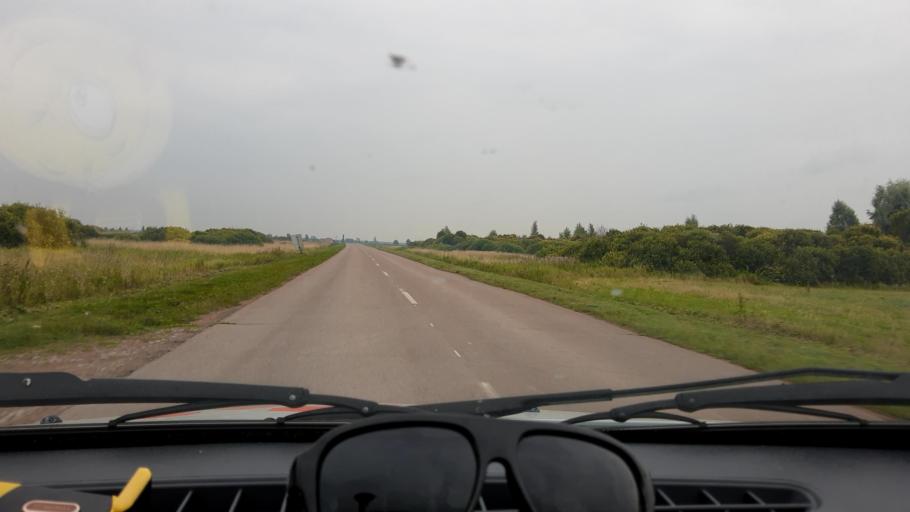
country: RU
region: Bashkortostan
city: Blagoveshchensk
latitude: 54.9941
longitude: 55.7576
